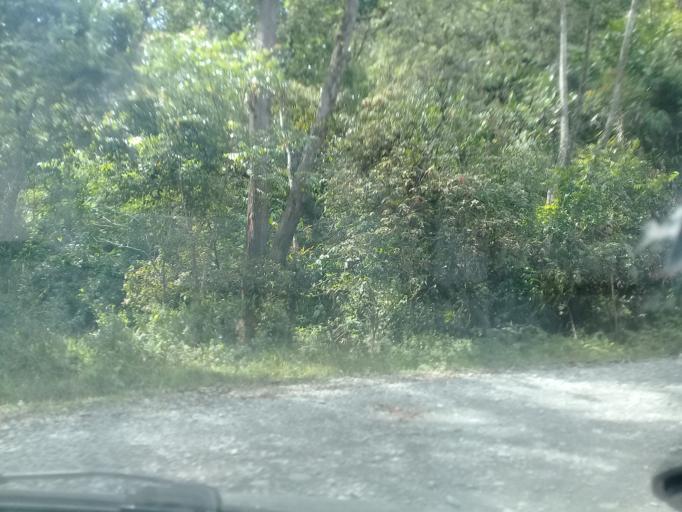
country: CO
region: Cundinamarca
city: Gachala
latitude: 4.6974
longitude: -73.4733
